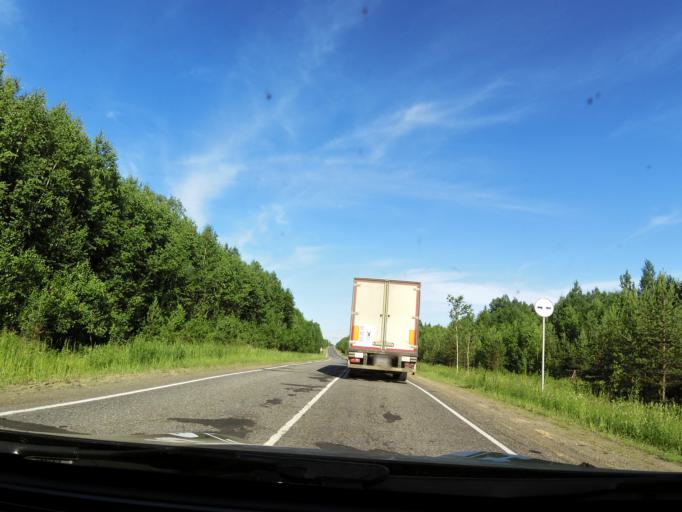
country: RU
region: Kirov
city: Chernaya Kholunitsa
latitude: 58.8748
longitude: 51.4894
